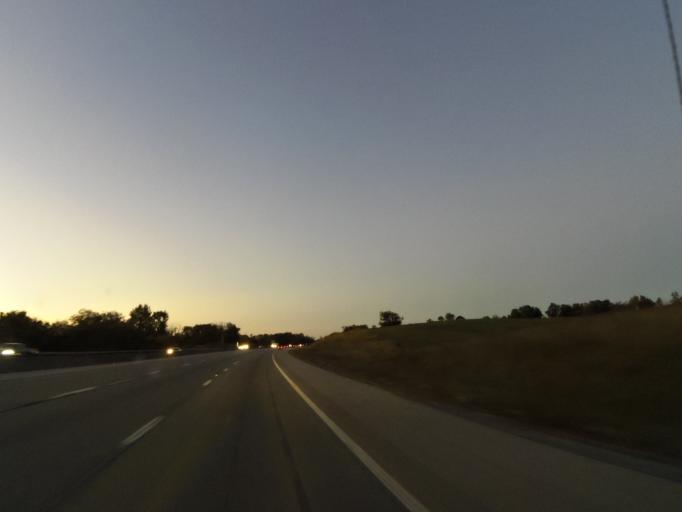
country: US
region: Kentucky
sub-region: Madison County
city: Berea
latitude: 37.6262
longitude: -84.3173
